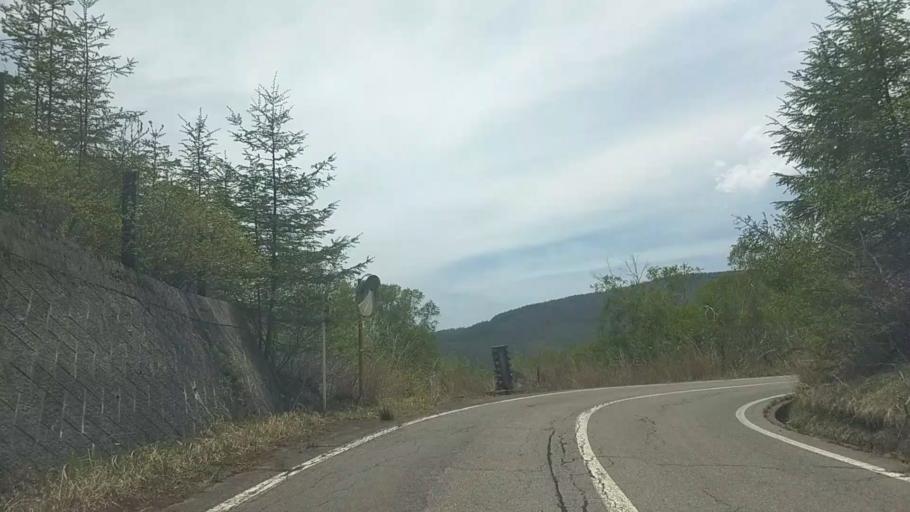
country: JP
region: Nagano
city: Saku
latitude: 36.0848
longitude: 138.3866
